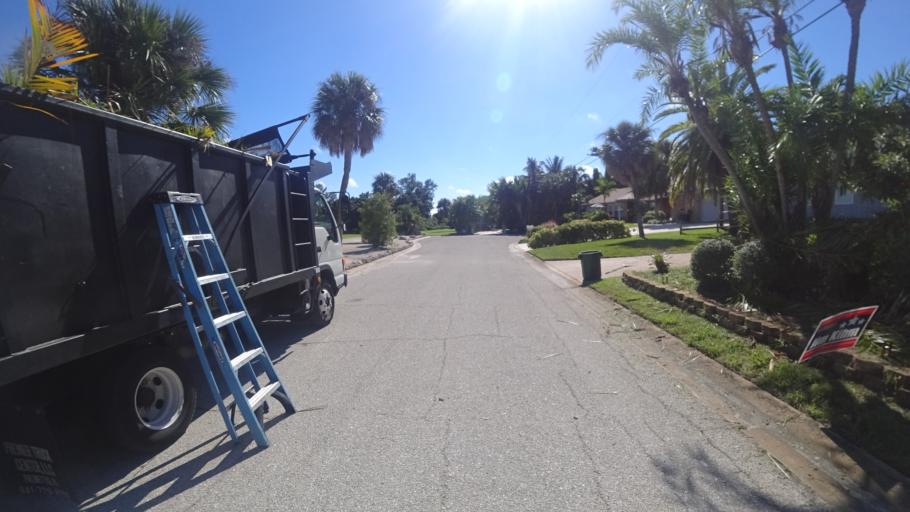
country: US
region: Florida
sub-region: Manatee County
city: Anna Maria
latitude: 27.5232
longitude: -82.7171
